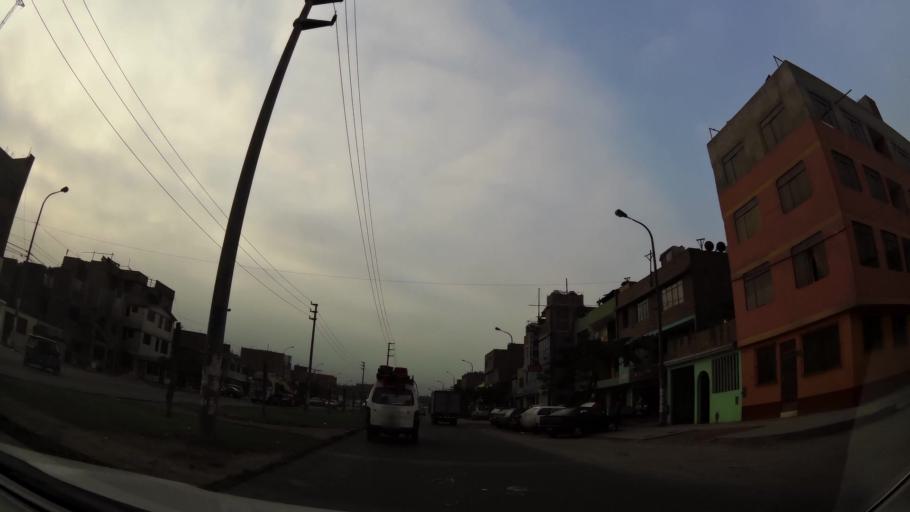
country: PE
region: Lima
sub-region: Lima
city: Independencia
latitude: -11.9951
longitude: -77.0006
